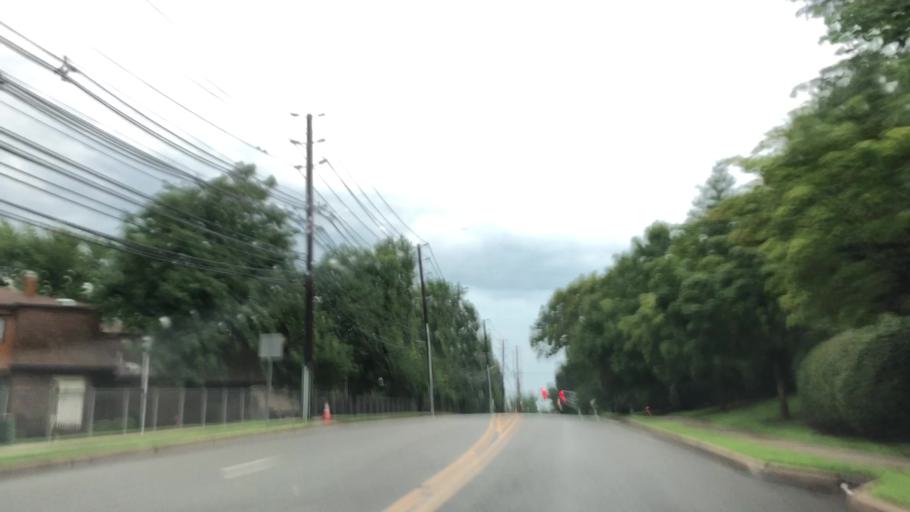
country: US
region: New Jersey
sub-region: Bergen County
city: Lyndhurst
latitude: 40.8247
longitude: -74.1343
